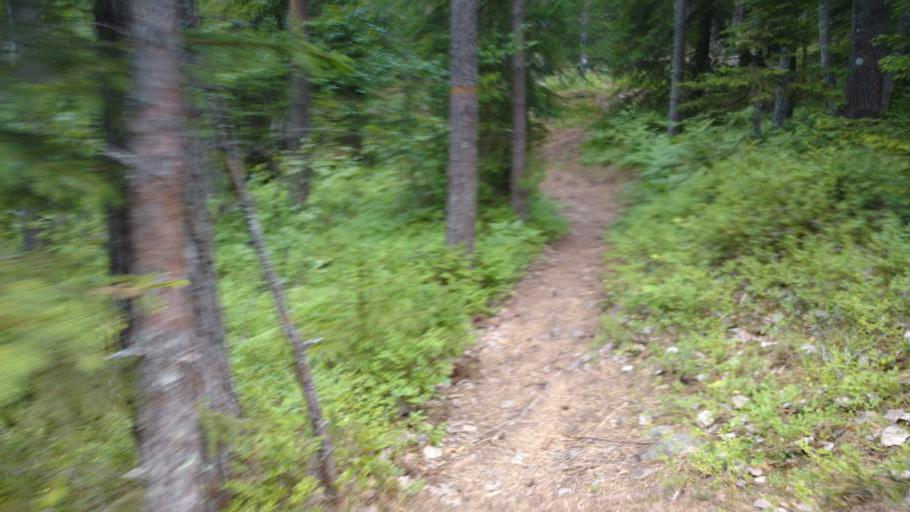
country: FI
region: Uusimaa
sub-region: Raaseporin
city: Pohja
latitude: 60.1133
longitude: 23.5607
